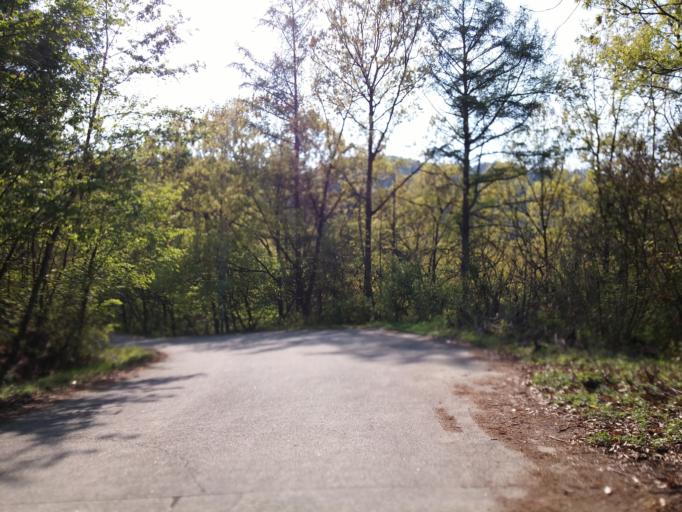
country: KR
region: Daejeon
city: Sintansin
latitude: 36.4218
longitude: 127.4859
